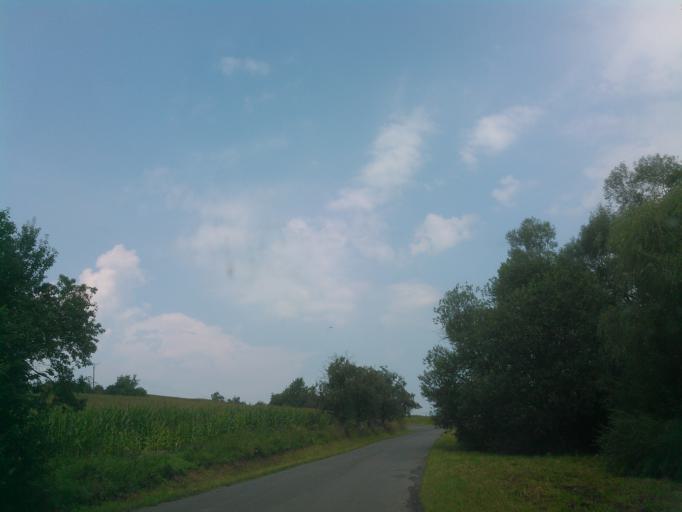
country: SK
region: Zilinsky
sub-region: Okres Liptovsky Mikulas
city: Liptovsky Mikulas
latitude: 49.0438
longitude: 19.4919
